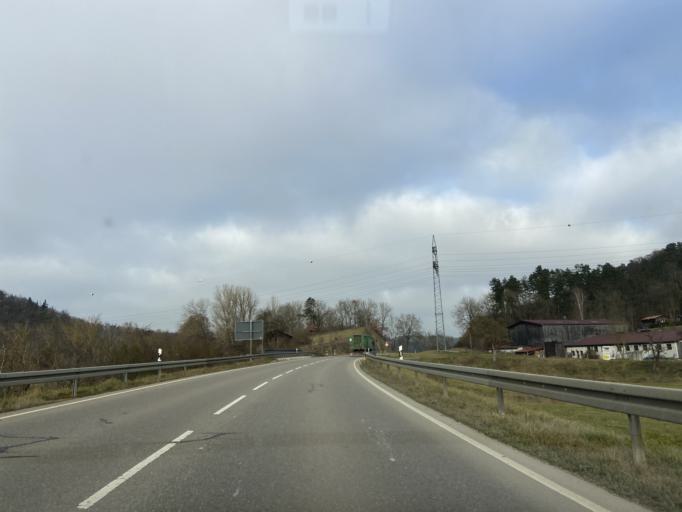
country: DE
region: Baden-Wuerttemberg
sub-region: Tuebingen Region
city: Veringenstadt
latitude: 48.1612
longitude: 9.2001
